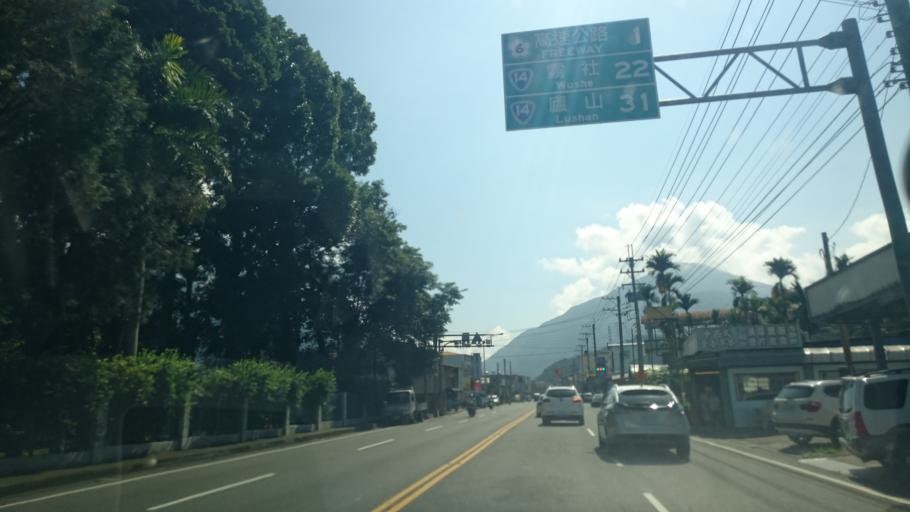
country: TW
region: Taiwan
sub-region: Nantou
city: Puli
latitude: 23.9761
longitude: 120.9847
